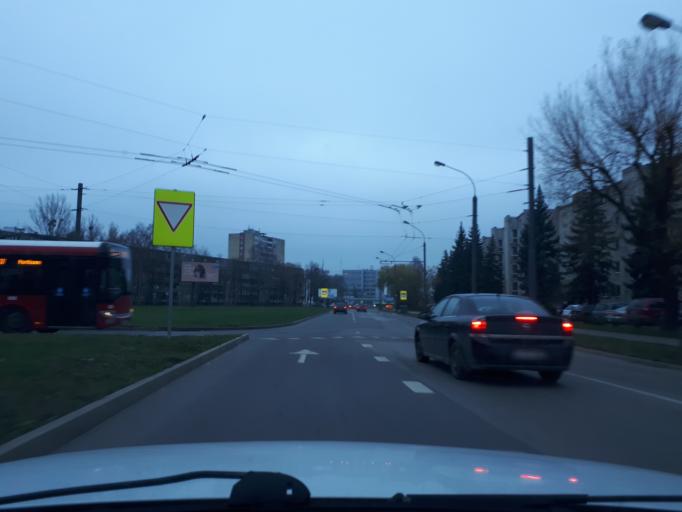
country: LT
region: Kauno apskritis
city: Dainava (Kaunas)
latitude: 54.9155
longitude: 23.9555
